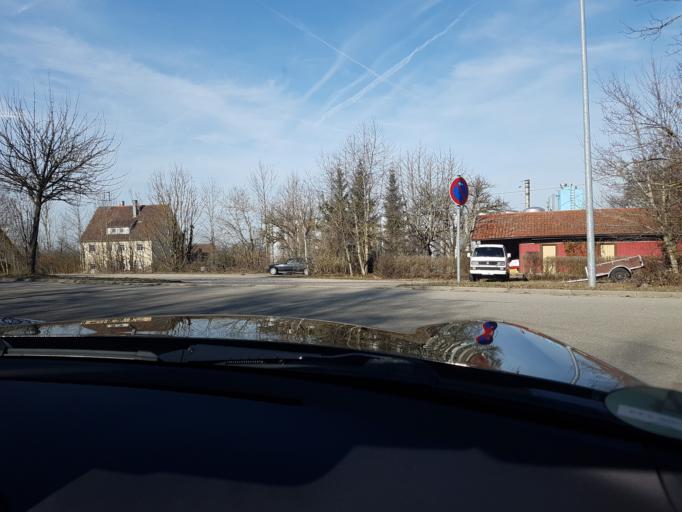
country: DE
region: Baden-Wuerttemberg
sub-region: Regierungsbezirk Stuttgart
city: Langenburg
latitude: 49.2541
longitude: 9.8581
